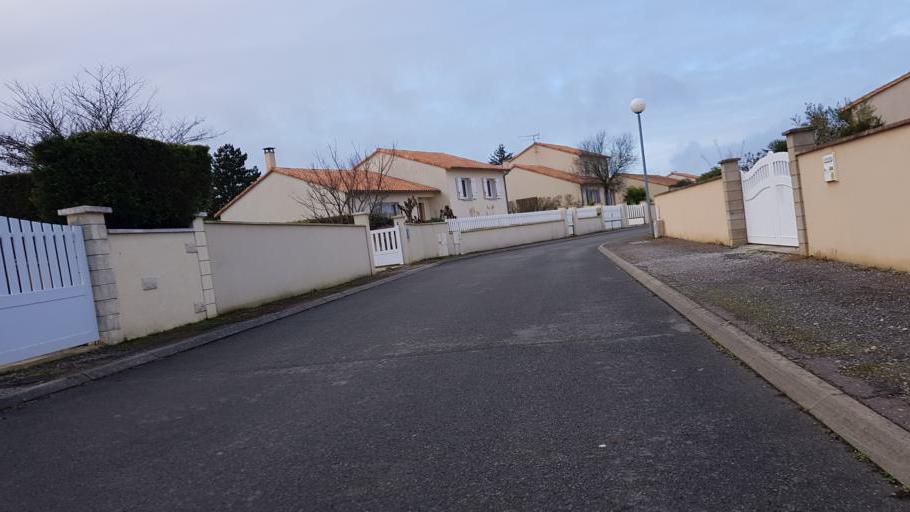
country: FR
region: Poitou-Charentes
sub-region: Departement de la Vienne
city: Avanton
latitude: 46.6650
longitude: 0.3132
